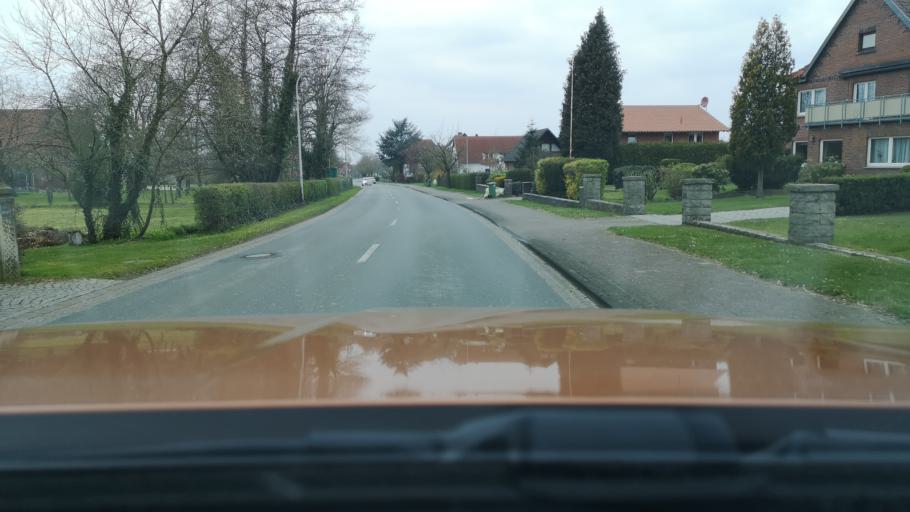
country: DE
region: Lower Saxony
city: Obernkirchen
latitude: 52.2842
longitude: 9.1184
